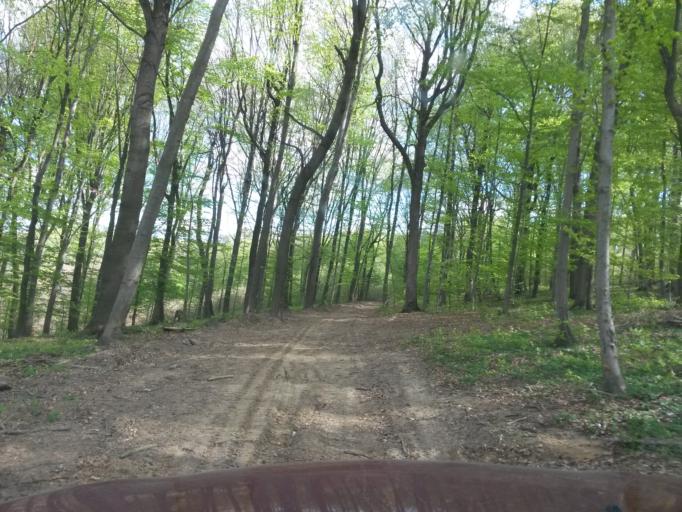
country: SK
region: Presovsky
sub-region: Okres Presov
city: Presov
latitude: 48.9540
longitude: 21.1325
